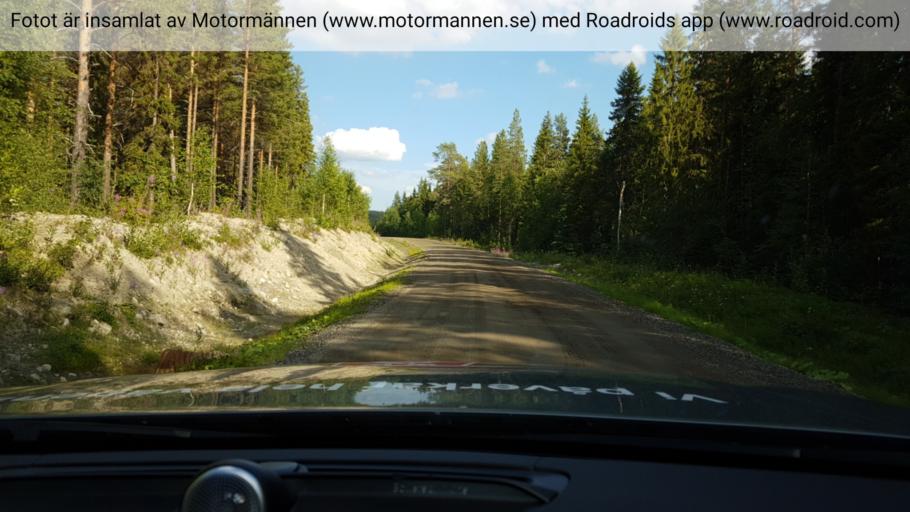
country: SE
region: Vaesterbotten
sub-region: Dorotea Kommun
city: Dorotea
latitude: 63.9293
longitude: 16.1209
